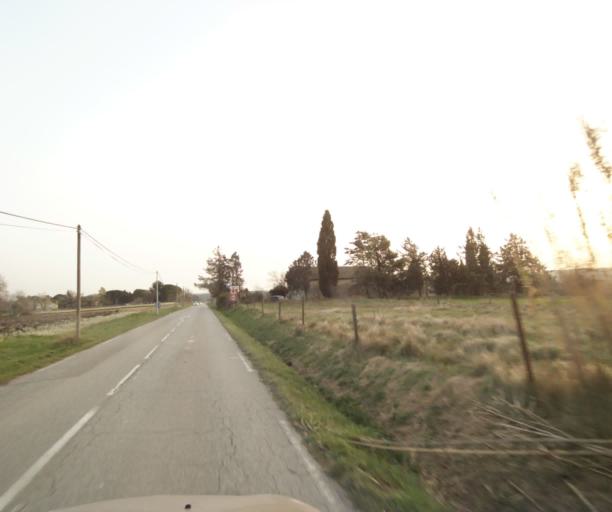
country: FR
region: Provence-Alpes-Cote d'Azur
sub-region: Departement des Bouches-du-Rhone
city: Eguilles
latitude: 43.5527
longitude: 5.3499
